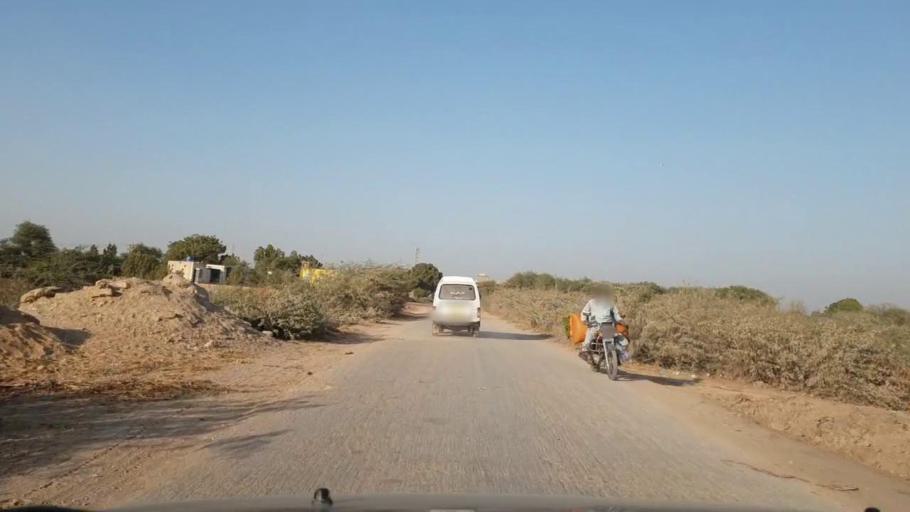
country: PK
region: Sindh
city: Chambar
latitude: 25.2846
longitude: 68.8107
